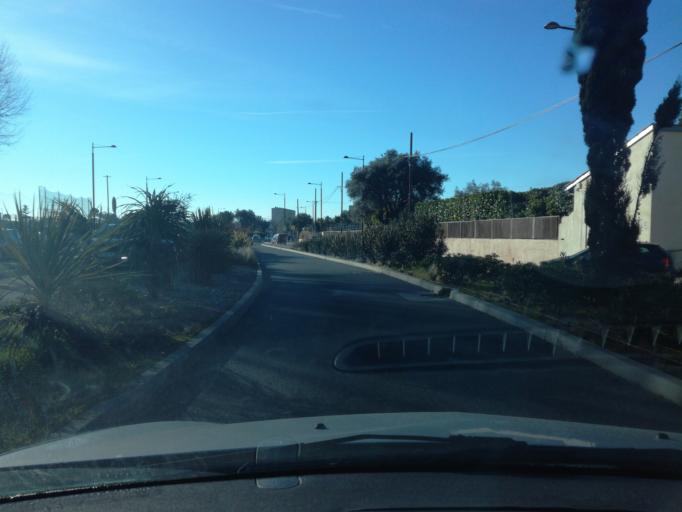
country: FR
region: Provence-Alpes-Cote d'Azur
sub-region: Departement des Alpes-Maritimes
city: Vallauris
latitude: 43.5825
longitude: 7.0896
